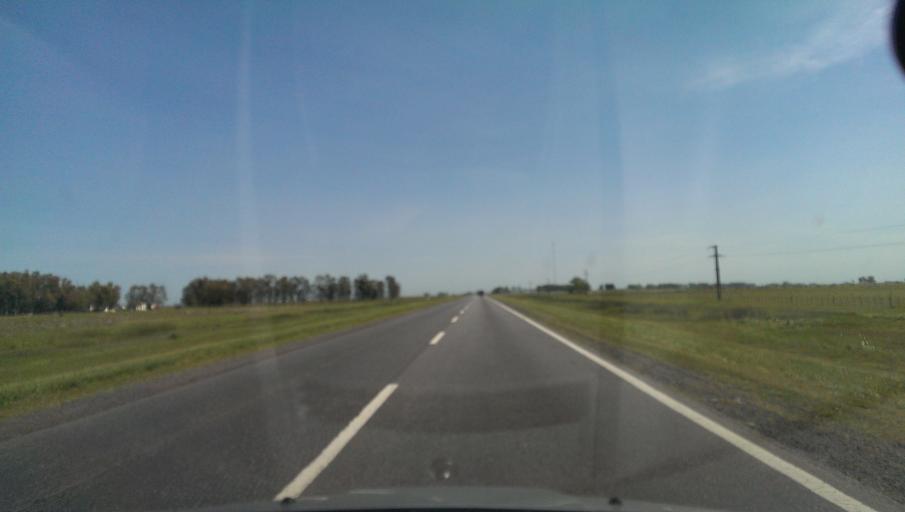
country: AR
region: Buenos Aires
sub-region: Partido de Azul
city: Azul
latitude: -36.5995
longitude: -59.6643
